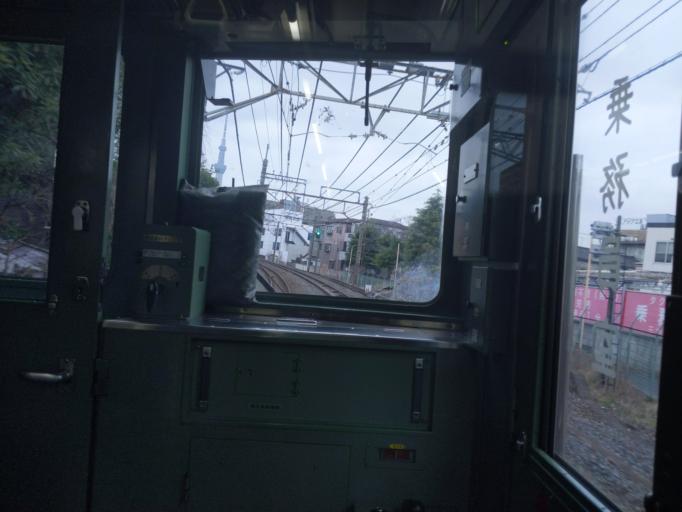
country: JP
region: Saitama
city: Soka
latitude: 35.7326
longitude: 139.8194
